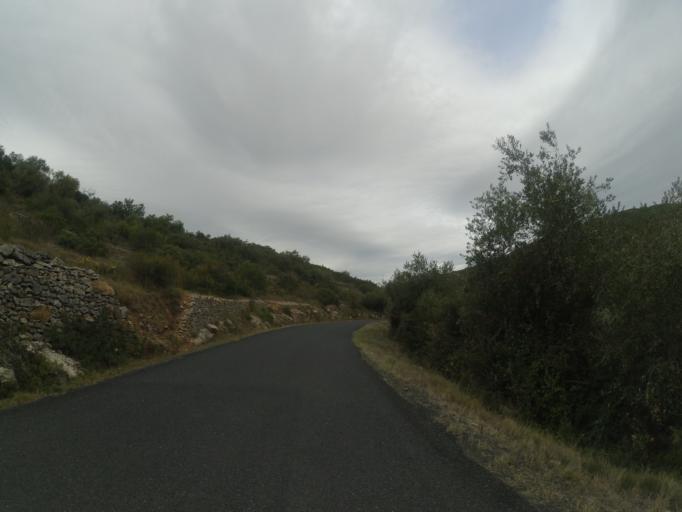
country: FR
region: Languedoc-Roussillon
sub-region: Departement des Pyrenees-Orientales
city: Estagel
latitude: 42.7672
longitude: 2.7036
